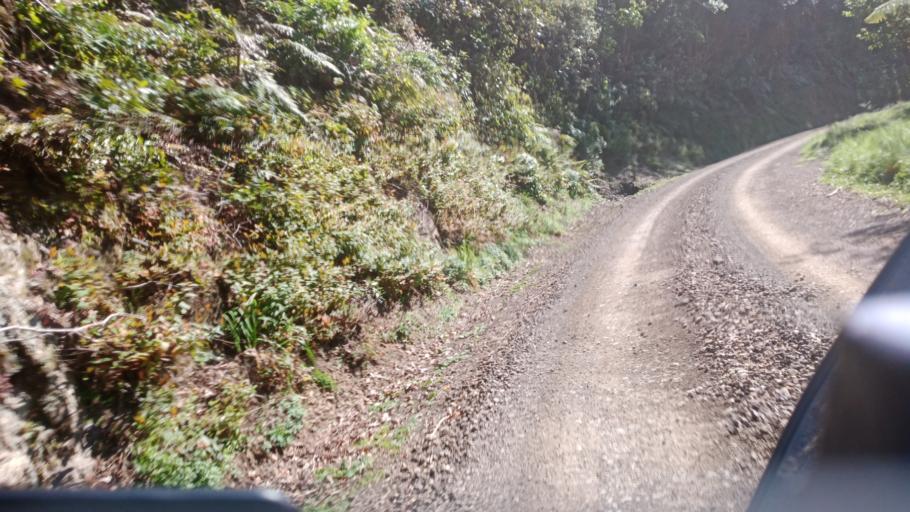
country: NZ
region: Bay of Plenty
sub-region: Opotiki District
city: Opotiki
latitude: -38.0876
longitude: 177.4786
